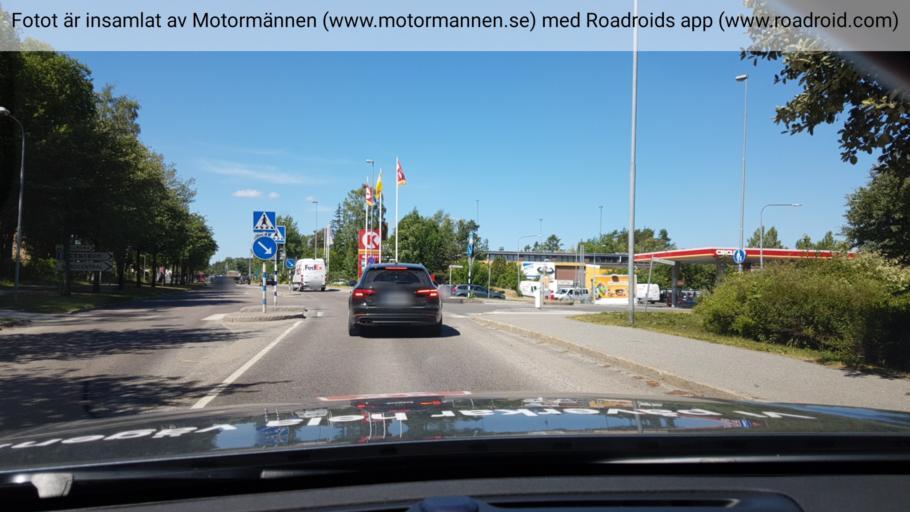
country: SE
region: Stockholm
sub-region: Tyreso Kommun
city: Bollmora
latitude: 59.2429
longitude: 18.2205
